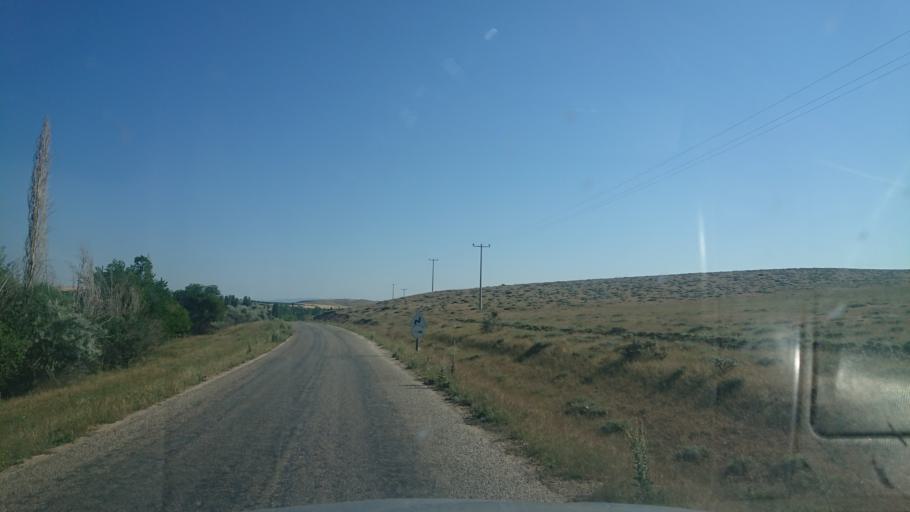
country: TR
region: Aksaray
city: Agacoren
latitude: 38.8753
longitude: 33.8806
